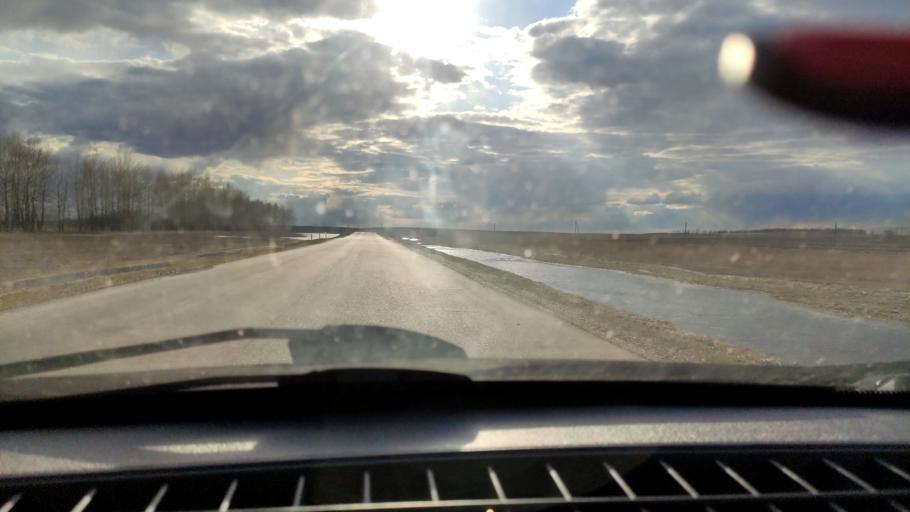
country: RU
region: Bashkortostan
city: Karmaskaly
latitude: 54.3461
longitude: 56.0310
